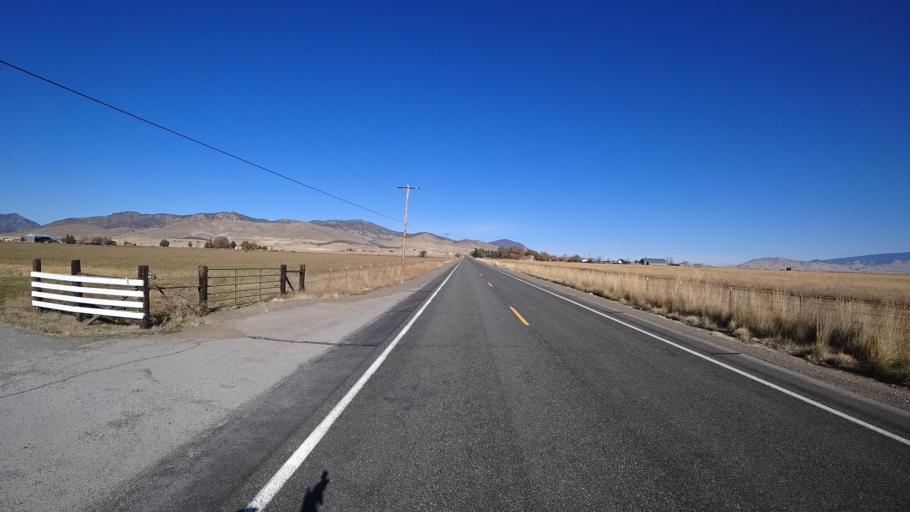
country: US
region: California
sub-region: Siskiyou County
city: Montague
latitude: 41.7603
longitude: -122.5247
